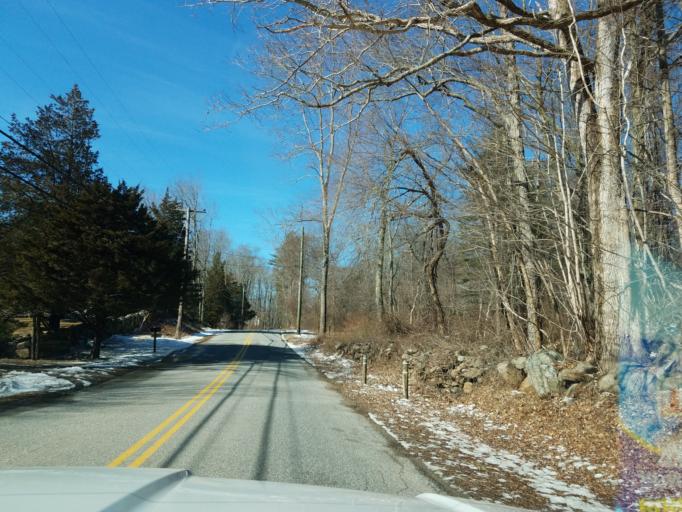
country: US
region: Connecticut
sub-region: New London County
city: Old Mystic
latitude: 41.4457
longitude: -71.9089
